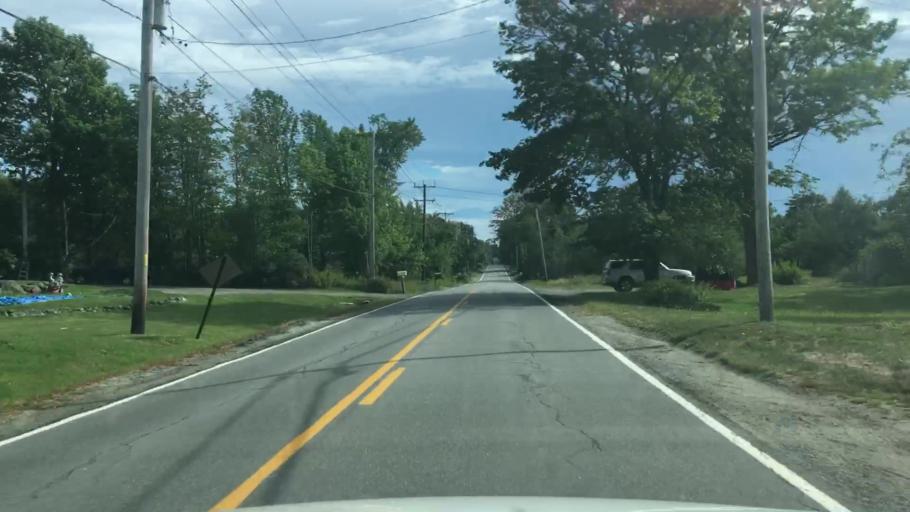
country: US
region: Maine
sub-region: Hancock County
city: Ellsworth
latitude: 44.4987
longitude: -68.4204
